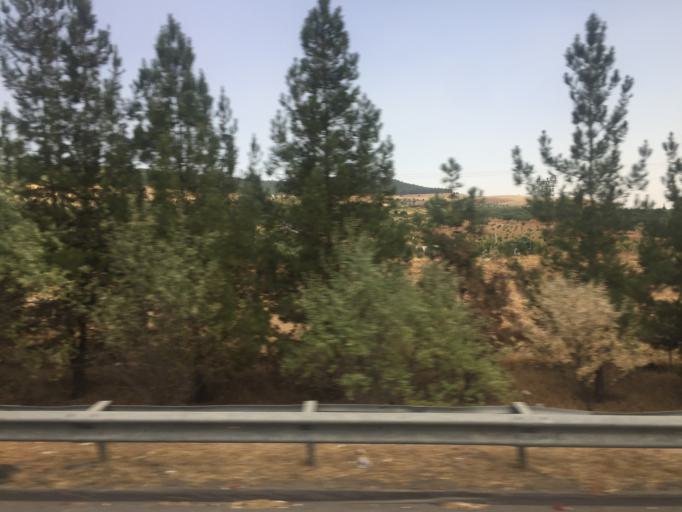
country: TR
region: Sanliurfa
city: Akziyaret
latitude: 37.2642
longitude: 38.7976
